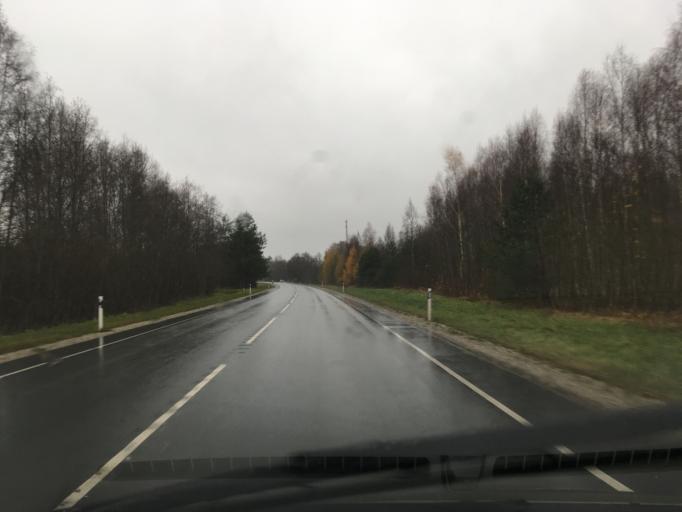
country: EE
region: Harju
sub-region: Nissi vald
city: Turba
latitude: 58.8903
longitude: 24.0943
